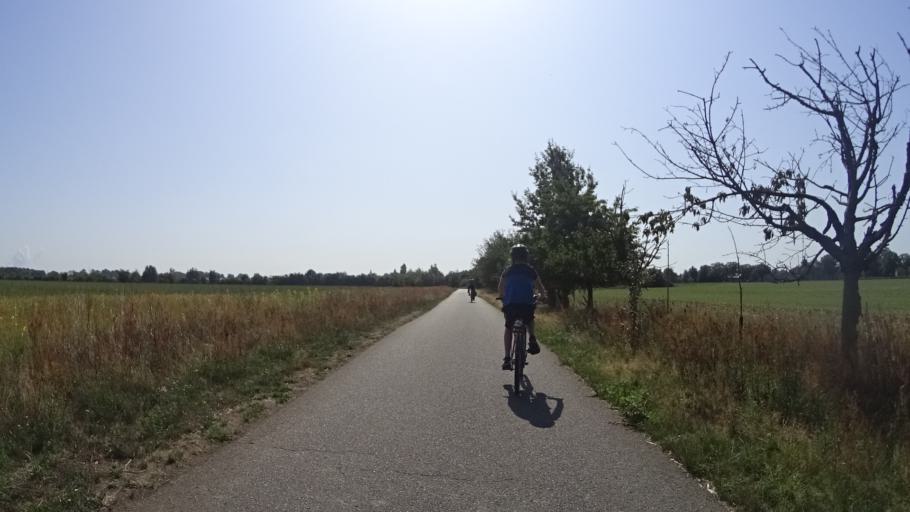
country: DE
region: Brandenburg
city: Werben
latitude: 51.8195
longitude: 14.1690
